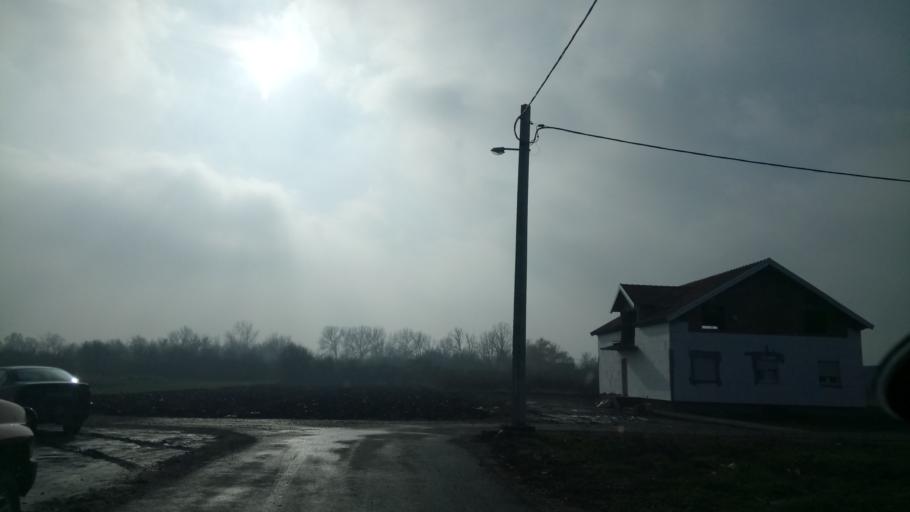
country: RS
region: Autonomna Pokrajina Vojvodina
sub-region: Sremski Okrug
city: Stara Pazova
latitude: 44.9770
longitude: 20.1731
